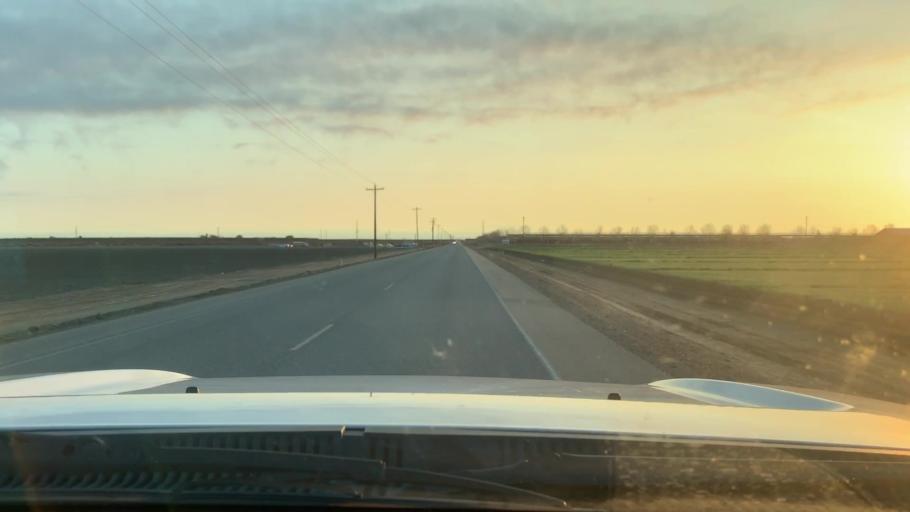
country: US
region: California
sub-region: Kern County
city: Buttonwillow
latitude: 35.5005
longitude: -119.4606
